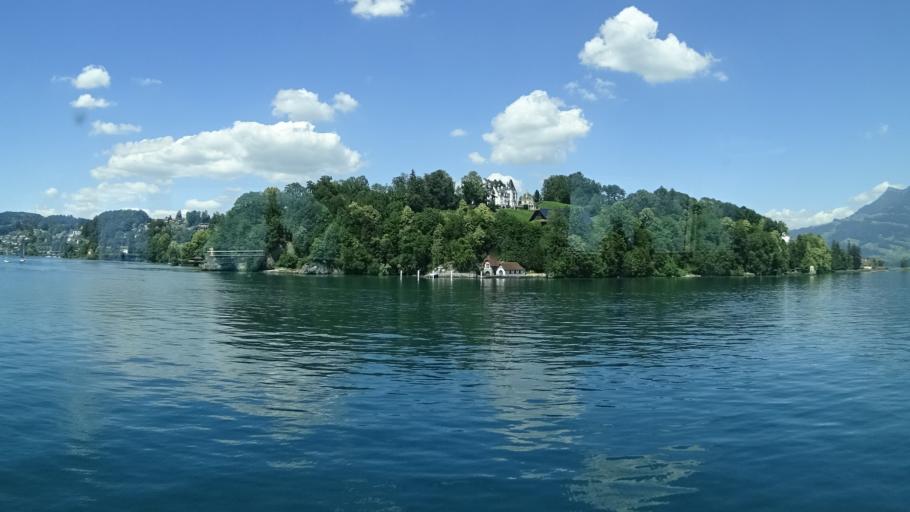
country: CH
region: Lucerne
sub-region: Lucerne-Land District
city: Meggen
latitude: 47.0317
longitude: 8.3527
